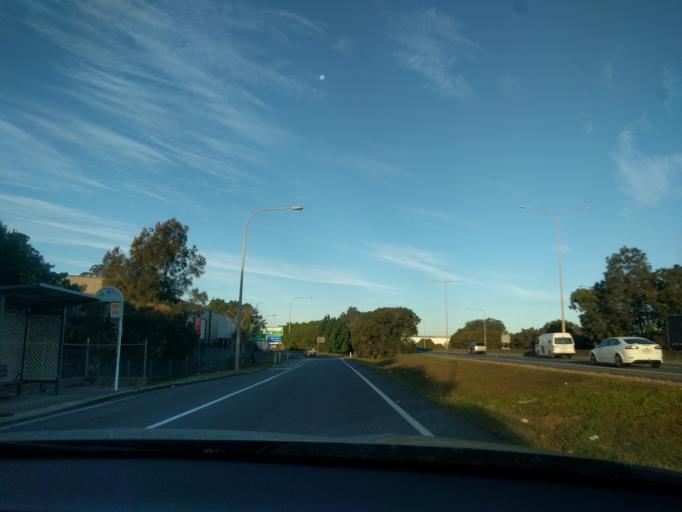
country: AU
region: Queensland
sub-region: Brisbane
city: Ascot
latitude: -27.4345
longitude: 153.0863
